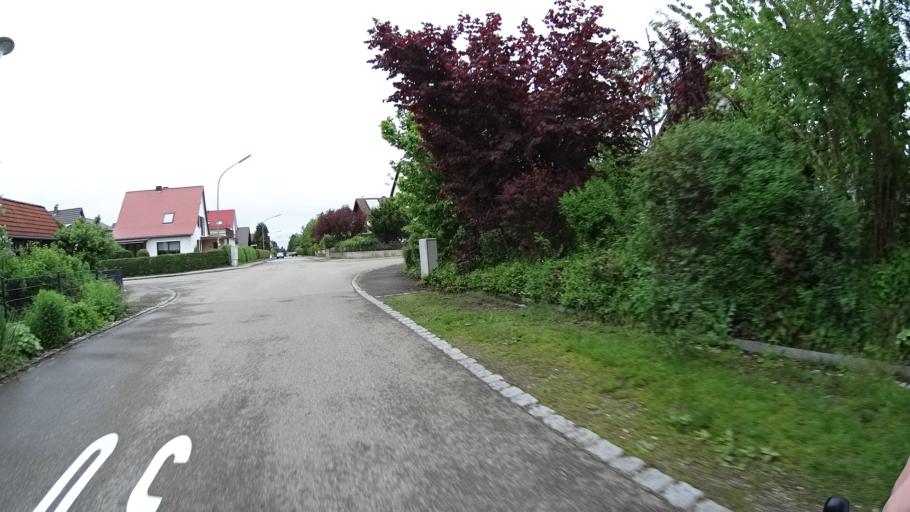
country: DE
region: Bavaria
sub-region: Swabia
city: Pfaffenhofen an der Roth
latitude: 48.3560
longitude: 10.1640
